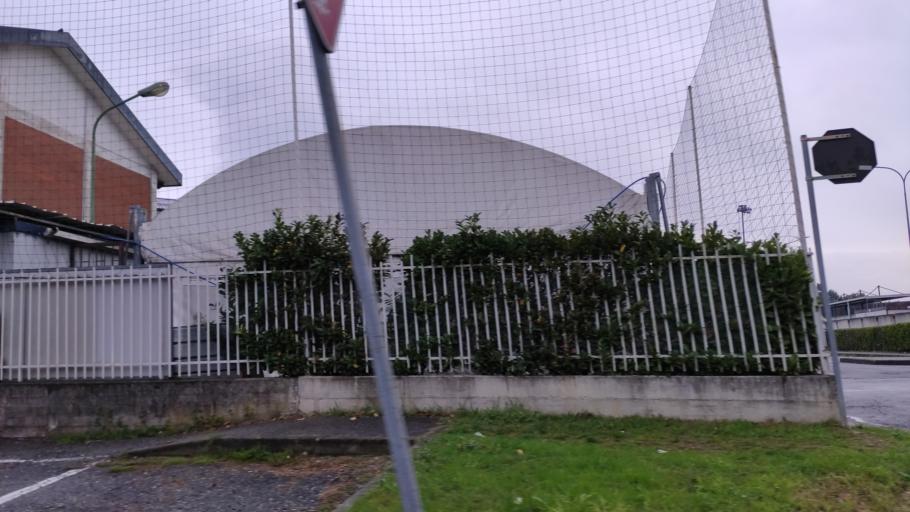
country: IT
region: Piedmont
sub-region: Provincia di Torino
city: Settimo Torinese
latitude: 45.1502
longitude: 7.7706
